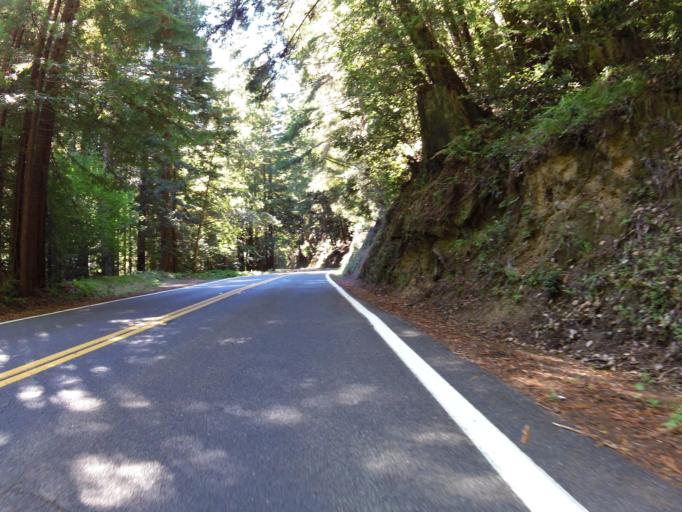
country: US
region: California
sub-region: Mendocino County
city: Fort Bragg
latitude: 39.7290
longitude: -123.8140
